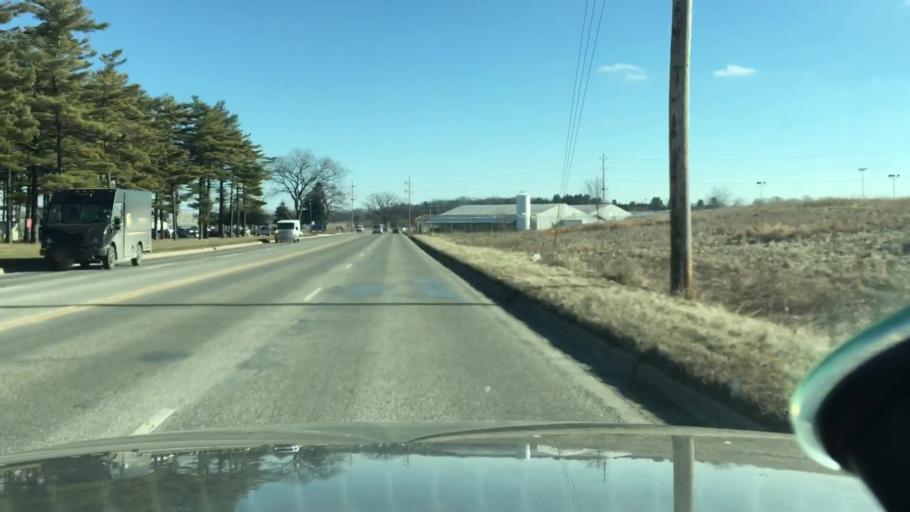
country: US
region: Michigan
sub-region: Jackson County
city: Jackson
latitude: 42.2911
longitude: -84.3939
